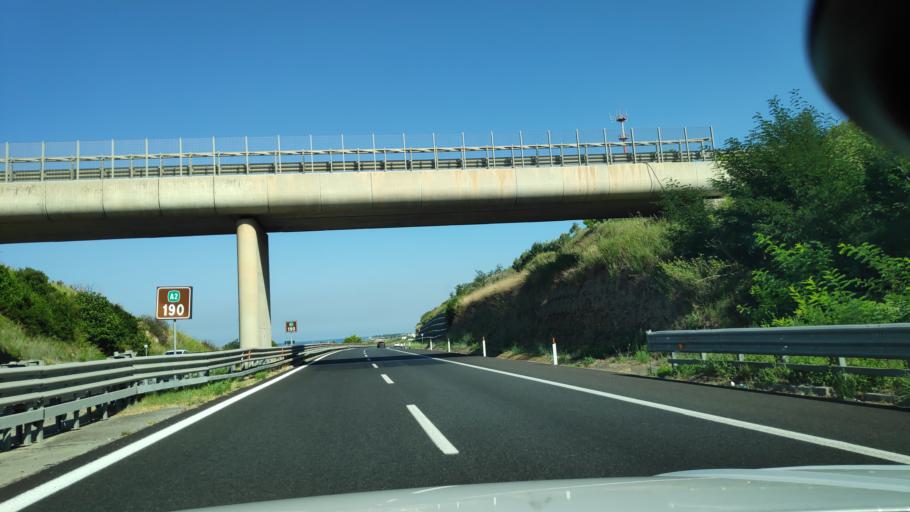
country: IT
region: Calabria
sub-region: Provincia di Catanzaro
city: Falerna Scalo
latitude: 38.9871
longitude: 16.1414
